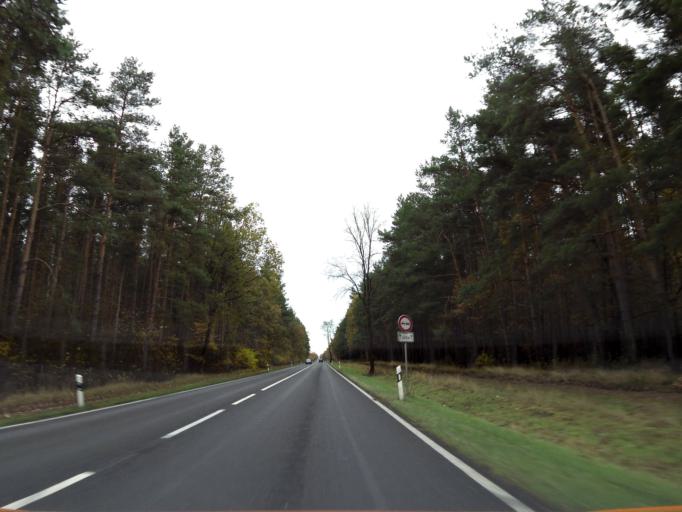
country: DE
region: Saxony-Anhalt
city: Letzlingen
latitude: 52.3879
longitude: 11.4687
